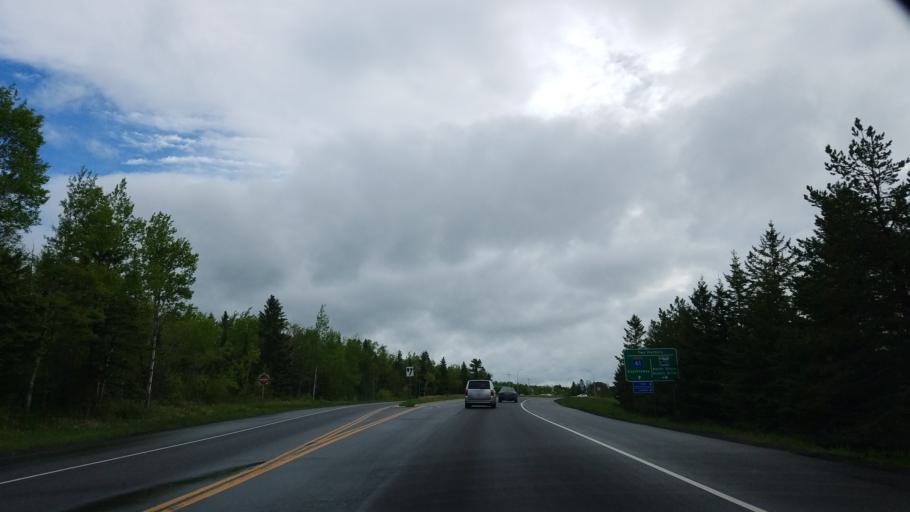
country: US
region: Minnesota
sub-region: Saint Louis County
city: Arnold
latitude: 46.8395
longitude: -91.9998
